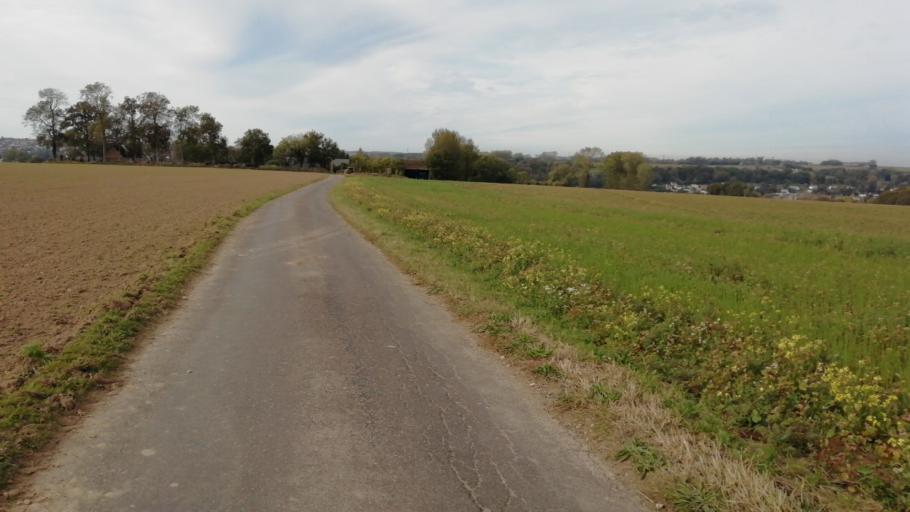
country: FR
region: Haute-Normandie
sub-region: Departement de la Seine-Maritime
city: Epouville
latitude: 49.5426
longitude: 0.2138
